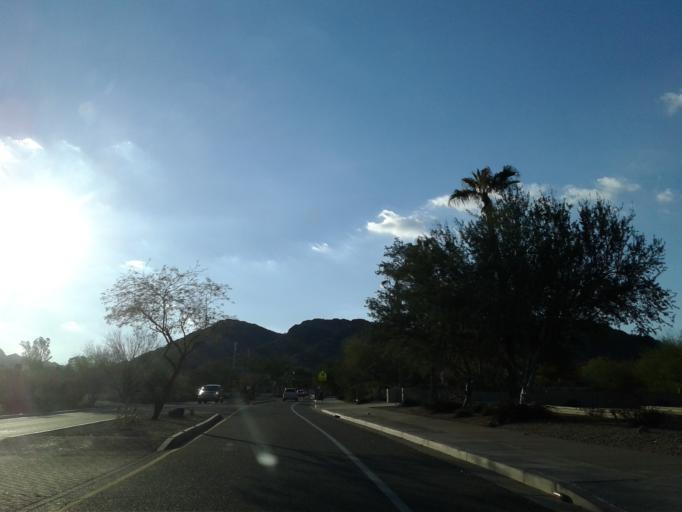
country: US
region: Arizona
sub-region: Maricopa County
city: Paradise Valley
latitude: 33.5683
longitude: -111.9748
